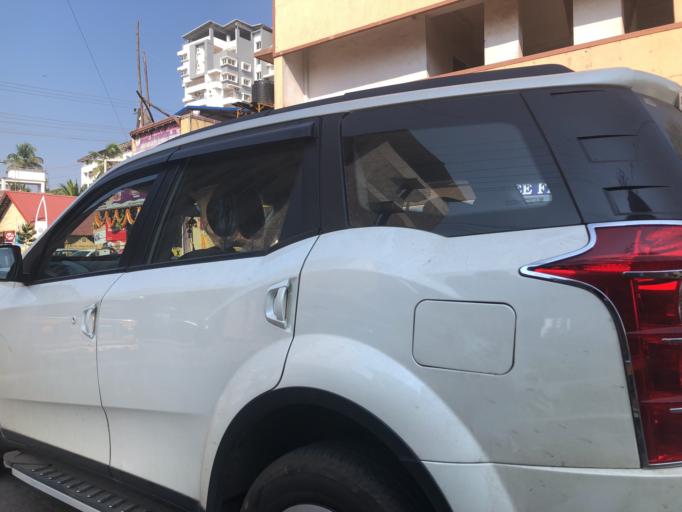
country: IN
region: Karnataka
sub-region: Dakshina Kannada
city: Mangalore
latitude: 12.8808
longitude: 74.8338
